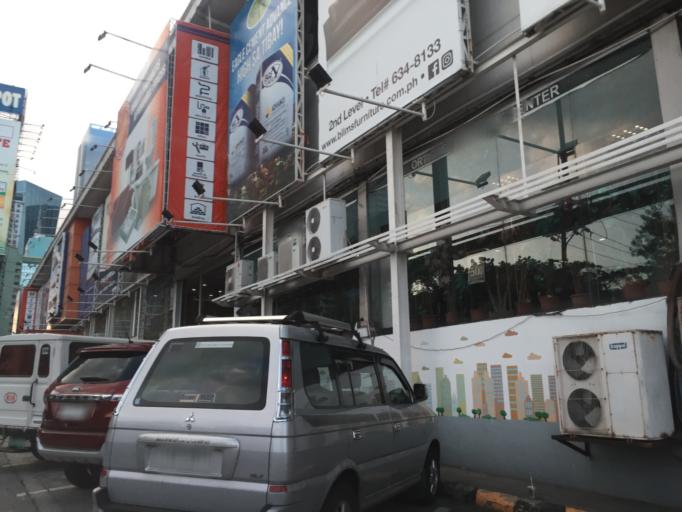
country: PH
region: Metro Manila
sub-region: Pasig
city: Pasig City
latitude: 14.5846
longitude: 121.0657
